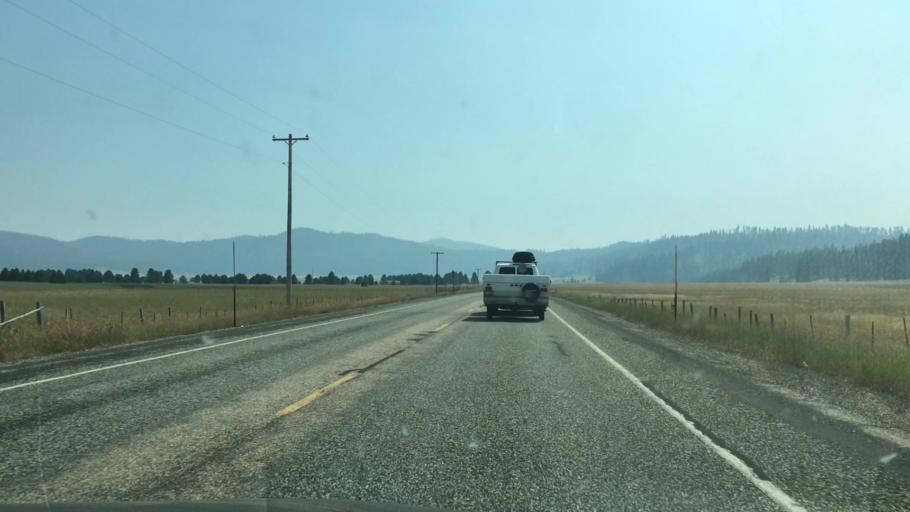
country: US
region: Idaho
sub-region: Valley County
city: Cascade
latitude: 44.3504
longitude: -116.0251
